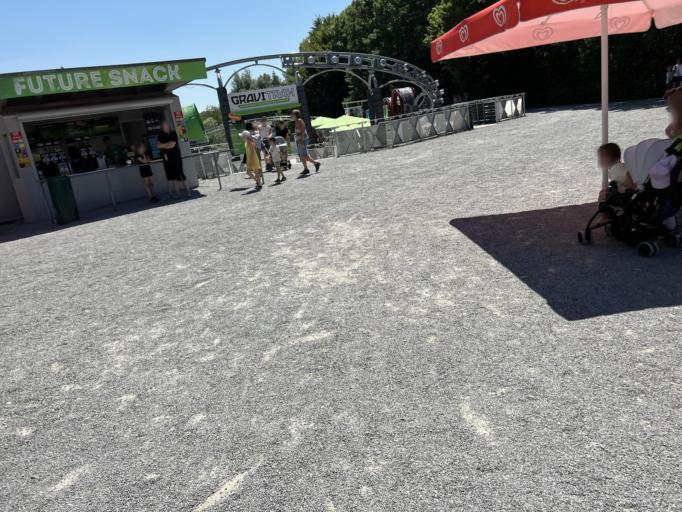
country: DE
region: Baden-Wuerttemberg
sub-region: Tuebingen Region
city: Meckenbeuren
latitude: 47.7124
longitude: 9.5955
